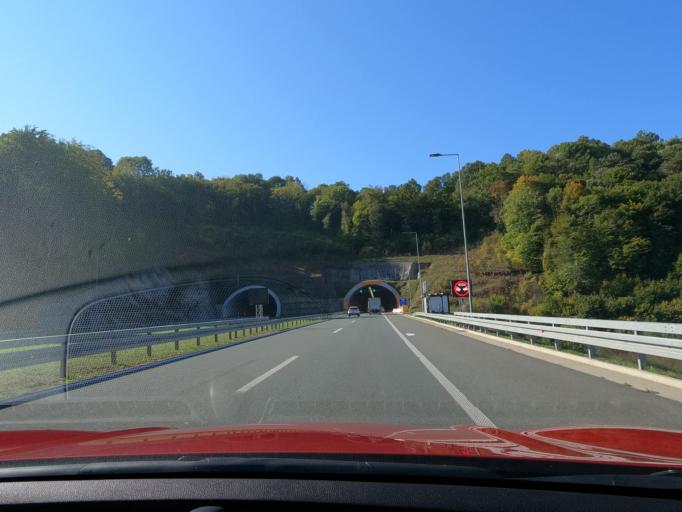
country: RS
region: Central Serbia
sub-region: Moravicki Okrug
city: Gornji Milanovac
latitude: 44.0279
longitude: 20.3640
